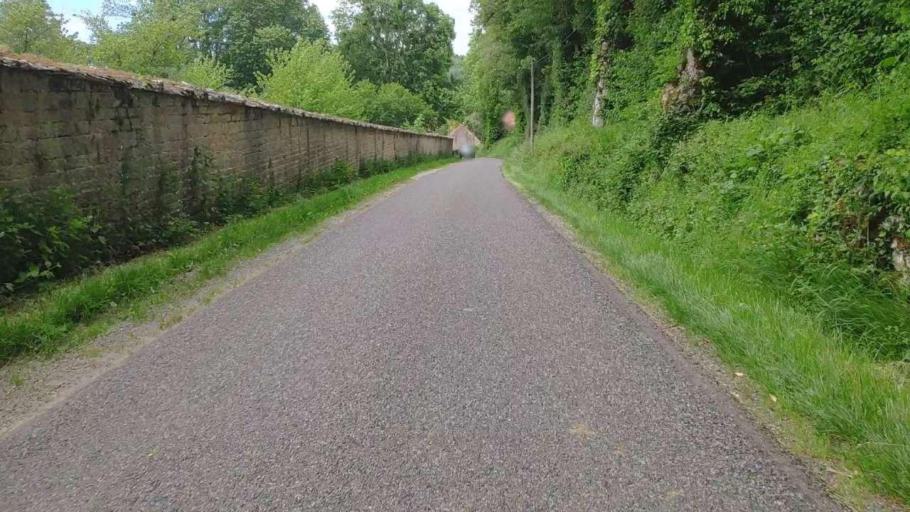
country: FR
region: Franche-Comte
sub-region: Departement du Jura
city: Montmorot
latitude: 46.7582
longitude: 5.5422
